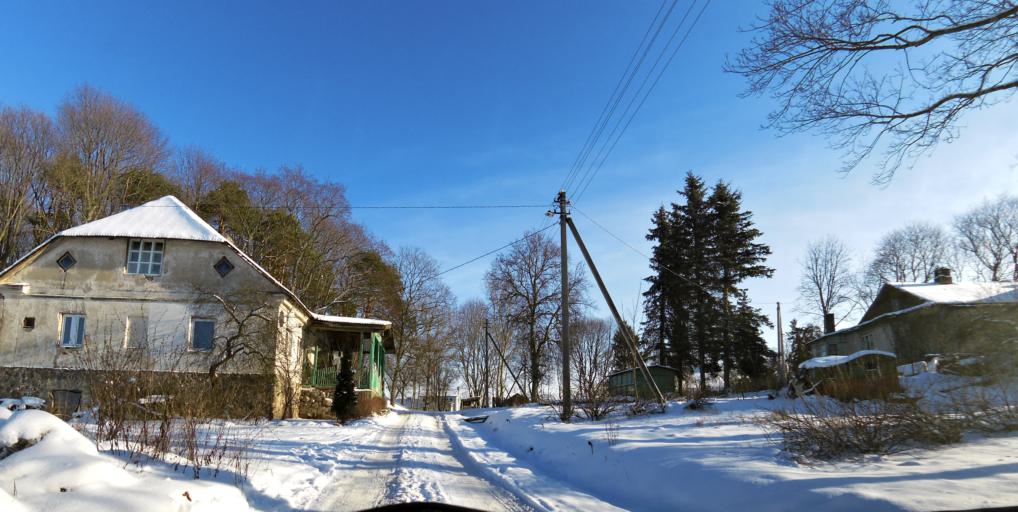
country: LT
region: Vilnius County
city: Pilaite
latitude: 54.7029
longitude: 25.1923
